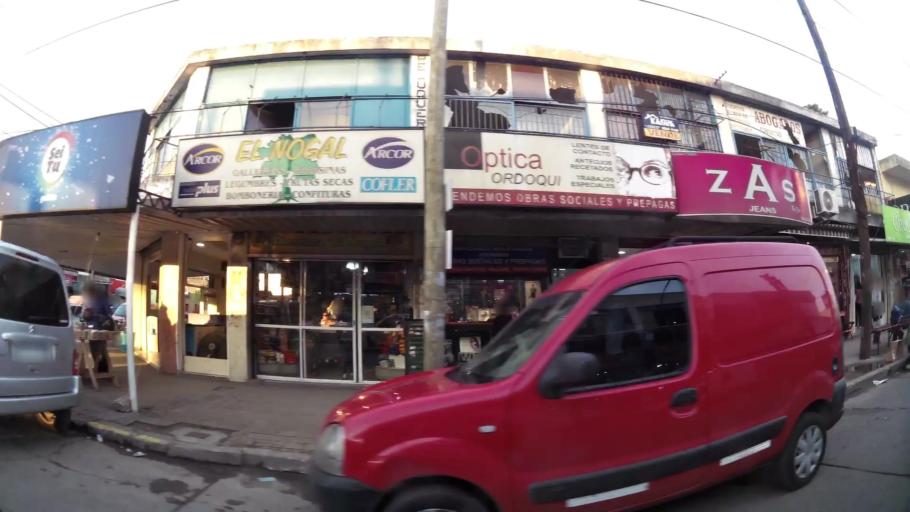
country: AR
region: Buenos Aires
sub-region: Partido de Almirante Brown
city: Adrogue
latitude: -34.7634
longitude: -58.3599
